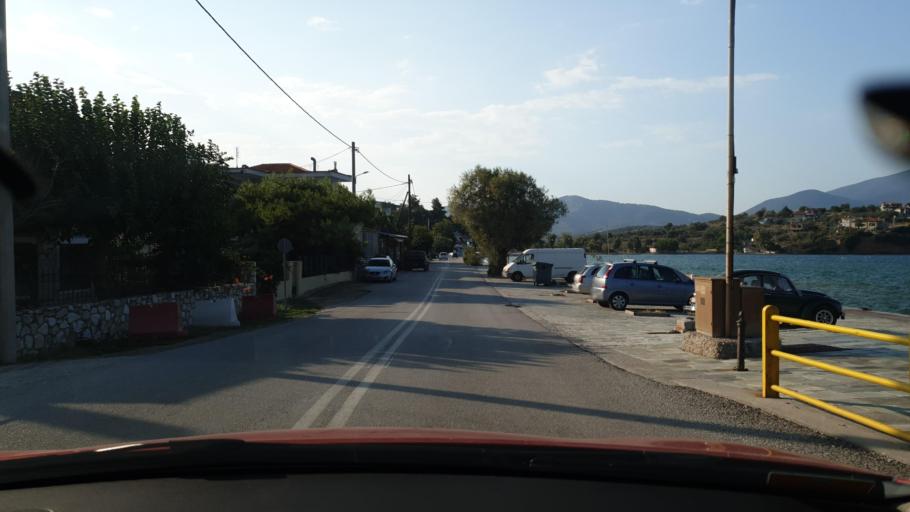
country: GR
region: Thessaly
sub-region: Nomos Magnisias
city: Pteleos
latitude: 39.0066
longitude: 22.9605
